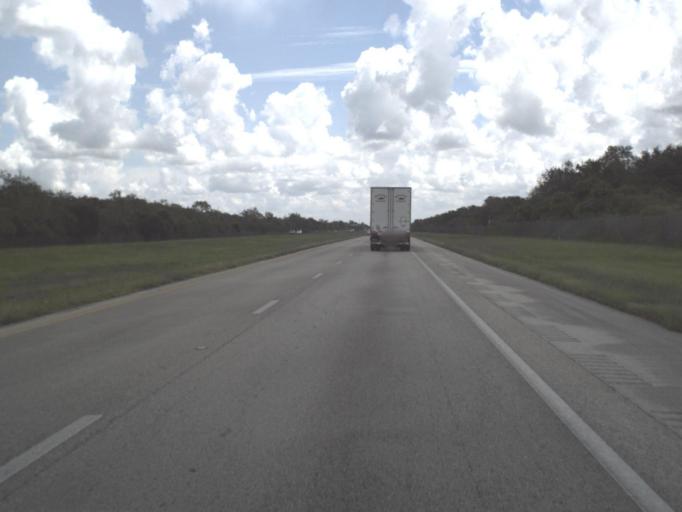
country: US
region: Florida
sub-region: Collier County
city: Orangetree
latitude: 26.1530
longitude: -81.5152
